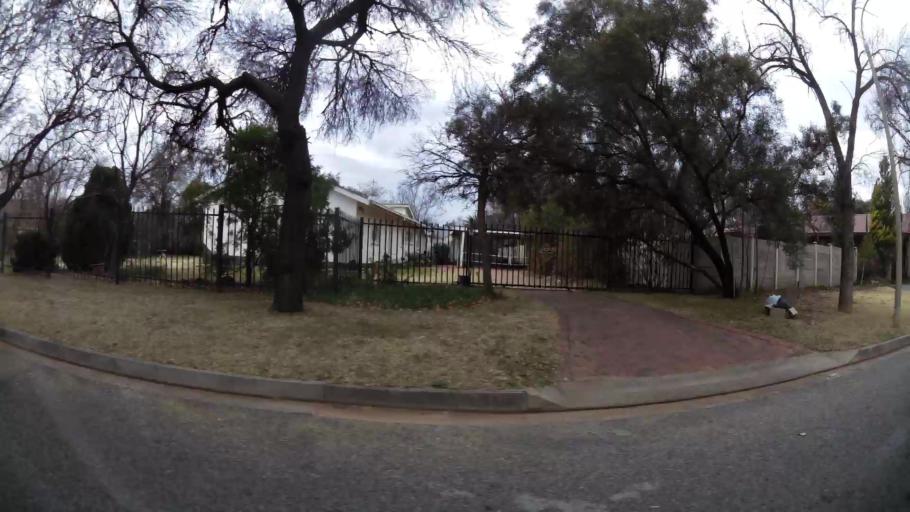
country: ZA
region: Orange Free State
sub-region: Fezile Dabi District Municipality
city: Kroonstad
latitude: -27.6777
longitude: 27.2476
